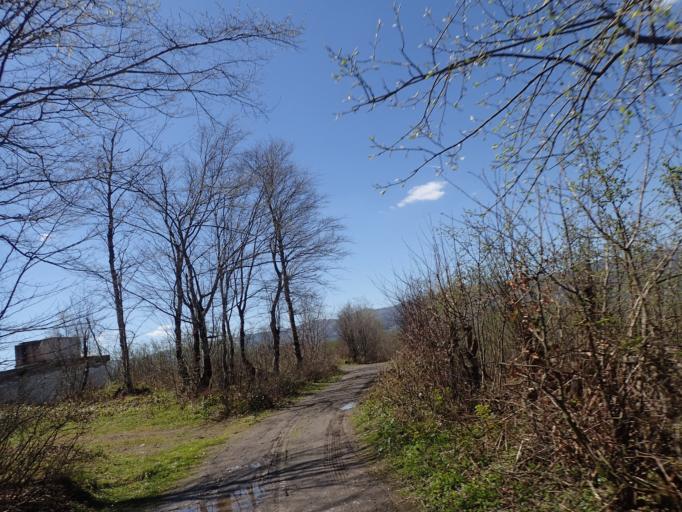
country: TR
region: Ordu
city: Korgan
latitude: 40.7606
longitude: 37.2995
